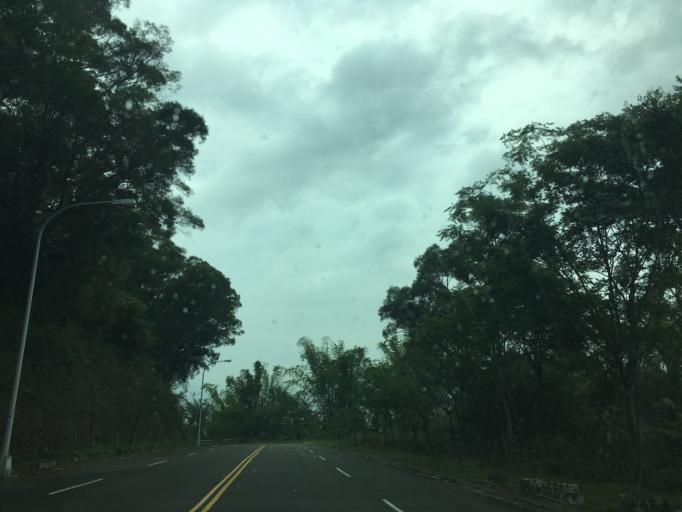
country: TW
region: Taiwan
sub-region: Taichung City
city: Taichung
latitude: 24.0628
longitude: 120.7251
